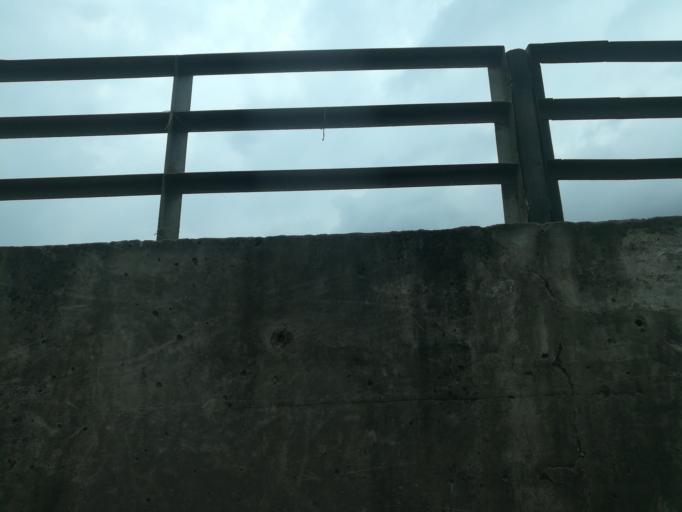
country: NG
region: Lagos
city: Ojota
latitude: 6.6078
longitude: 3.3936
